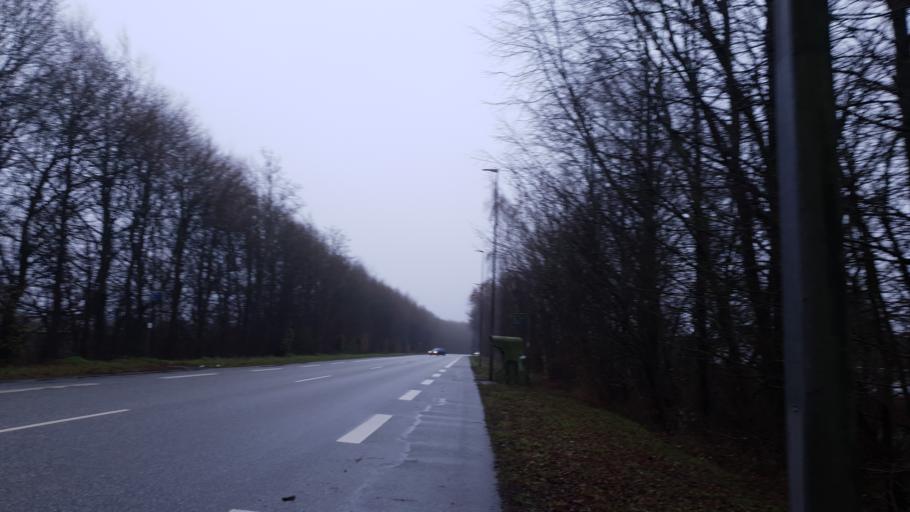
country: DK
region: Central Jutland
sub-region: Hedensted Kommune
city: Hedensted
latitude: 55.7895
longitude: 9.6996
